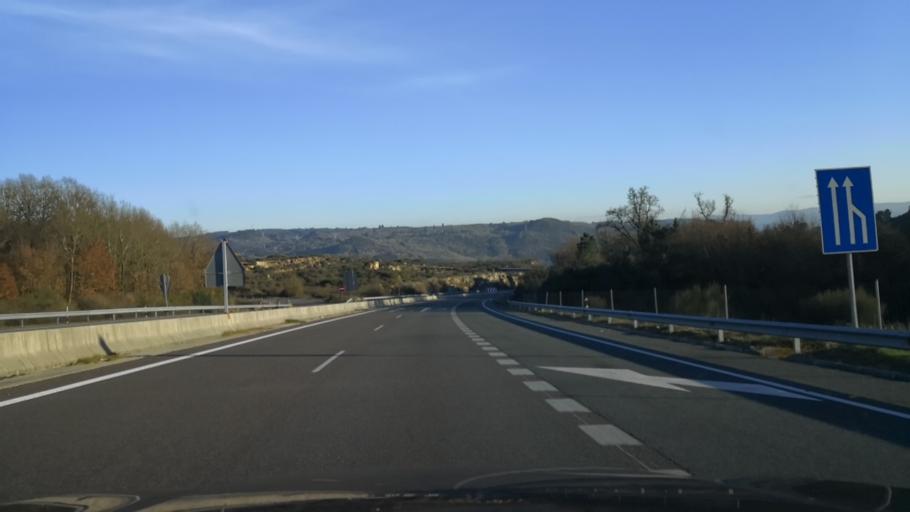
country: ES
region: Galicia
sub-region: Provincia de Ourense
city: Maside
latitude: 42.3981
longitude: -8.0014
